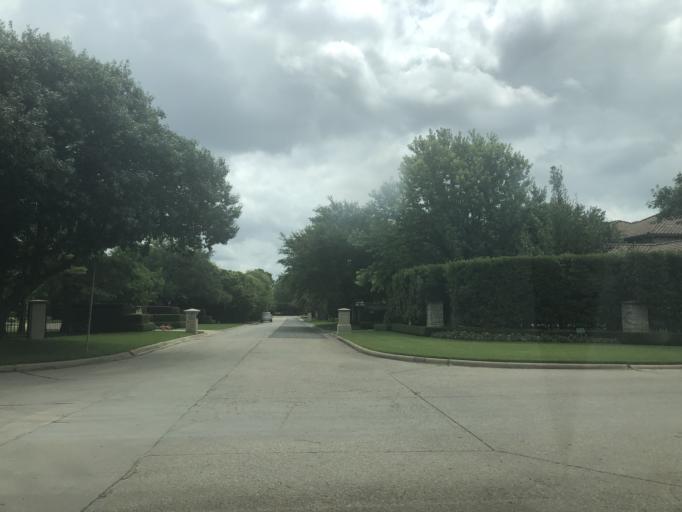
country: US
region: Texas
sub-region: Dallas County
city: University Park
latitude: 32.8897
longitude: -96.8299
